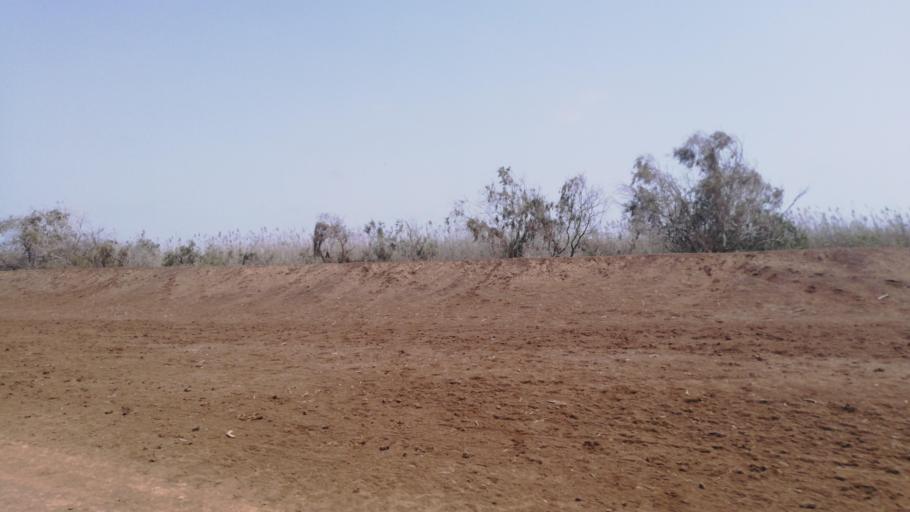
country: SN
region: Saint-Louis
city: Saint-Louis
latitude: 16.4015
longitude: -16.2908
